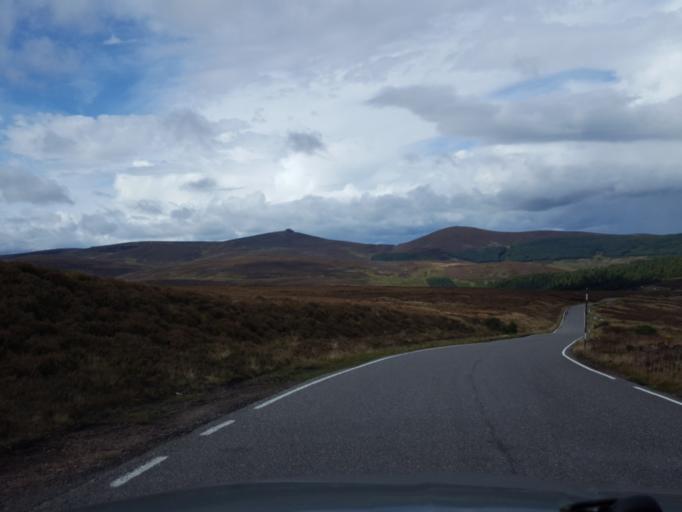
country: GB
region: Scotland
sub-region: Aberdeenshire
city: Banchory
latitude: 56.9357
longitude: -2.5723
